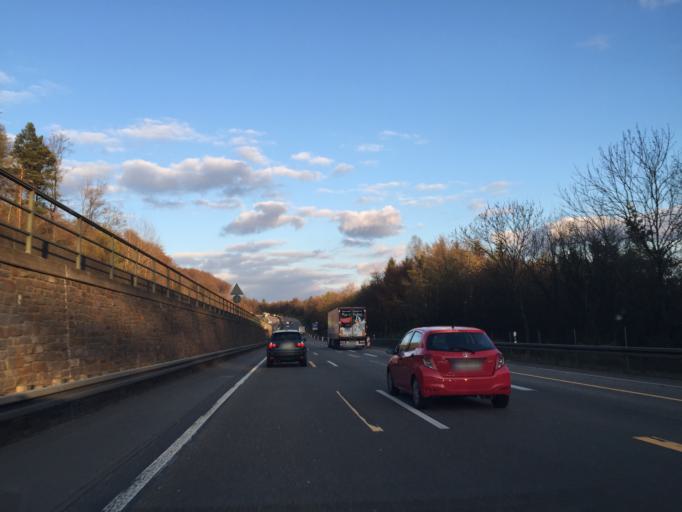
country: DE
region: Hesse
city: Grebenau
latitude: 50.7924
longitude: 9.4567
